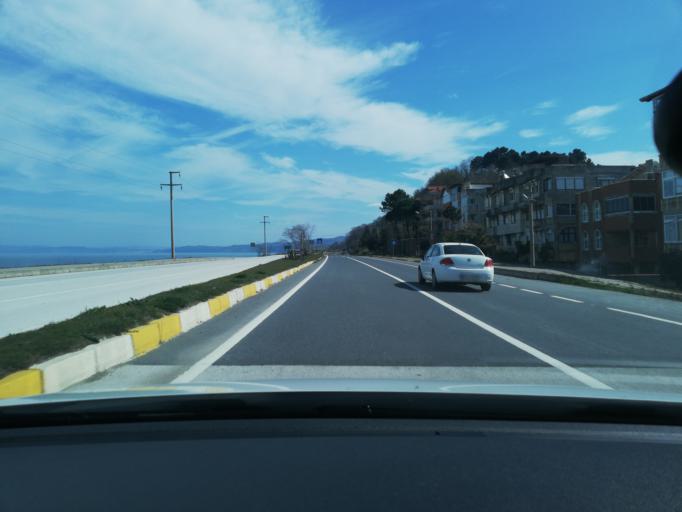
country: TR
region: Duzce
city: Akcakoca
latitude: 41.0952
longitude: 31.1982
